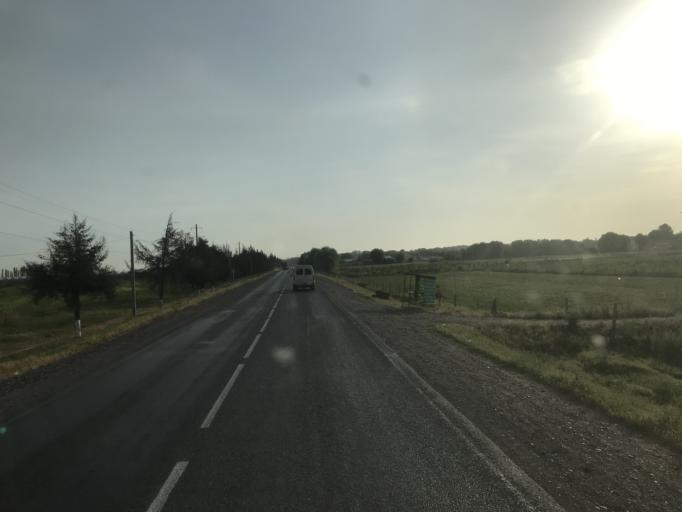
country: KZ
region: Ongtustik Qazaqstan
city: Saryaghash
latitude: 41.4838
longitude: 69.2535
